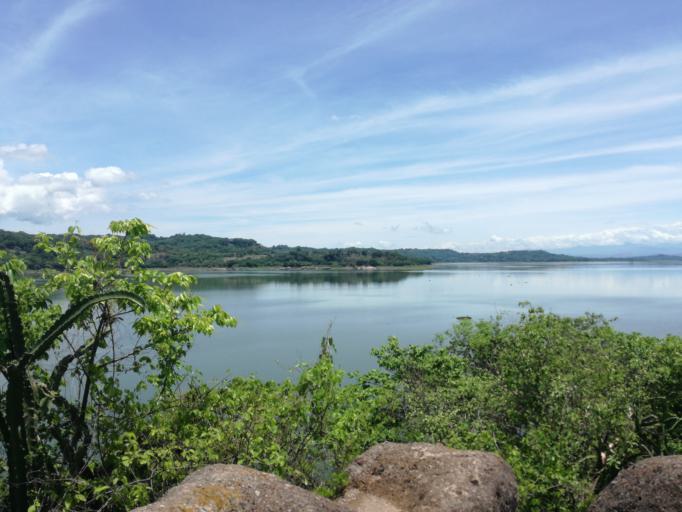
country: SV
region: Cuscatlan
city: Suchitoto
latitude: 13.9364
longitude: -88.9959
